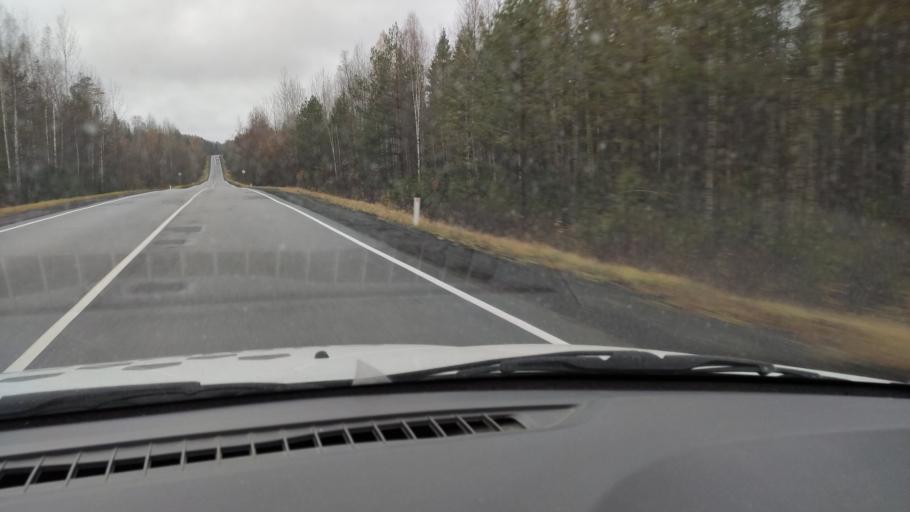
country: RU
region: Kirov
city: Chernaya Kholunitsa
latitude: 58.8637
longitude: 51.5911
